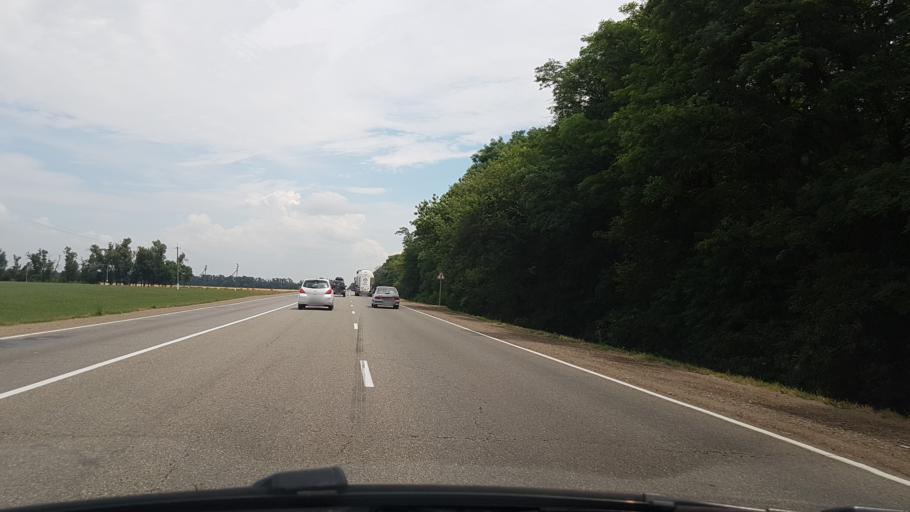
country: RU
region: Krasnodarskiy
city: Vasyurinskaya
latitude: 45.1627
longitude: 39.4650
